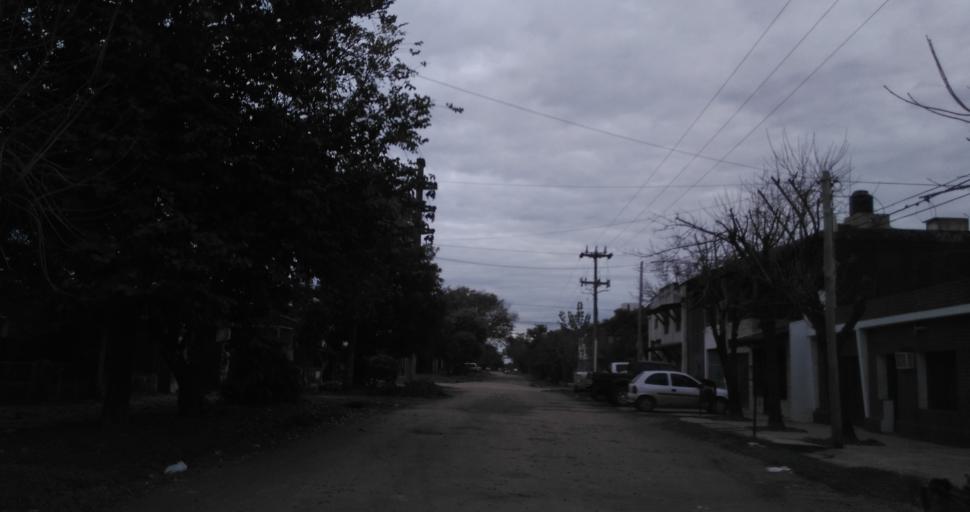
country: AR
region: Chaco
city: Resistencia
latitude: -27.4699
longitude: -58.9646
